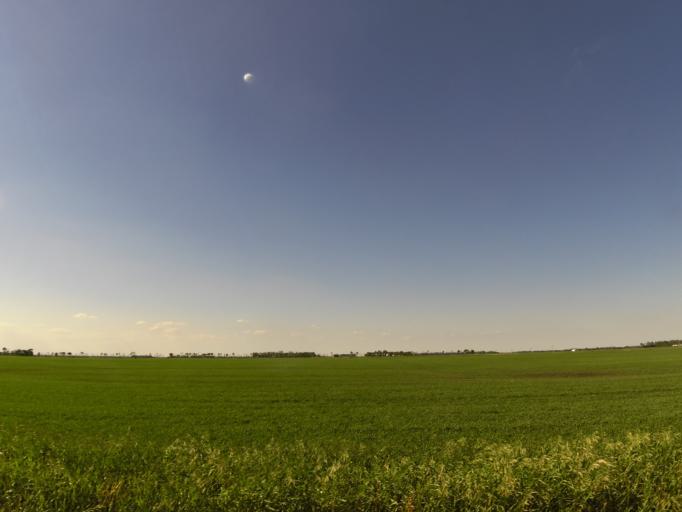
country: US
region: North Dakota
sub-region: Walsh County
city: Grafton
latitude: 48.3533
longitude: -97.2359
